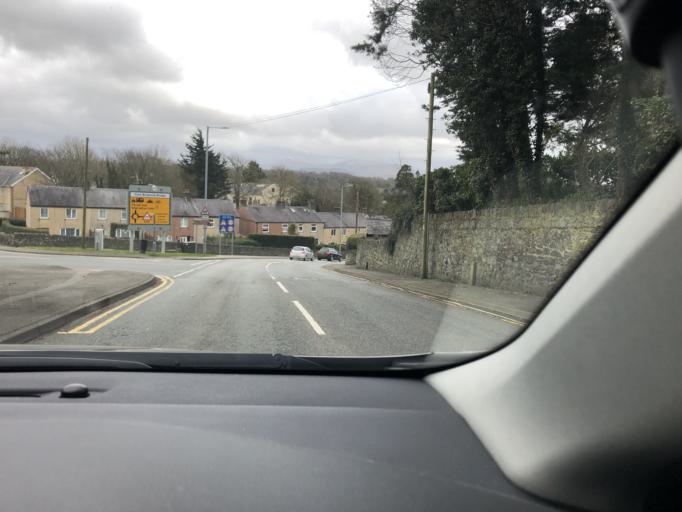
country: GB
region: Wales
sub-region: Anglesey
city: Menai Bridge
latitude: 53.2276
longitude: -4.1688
